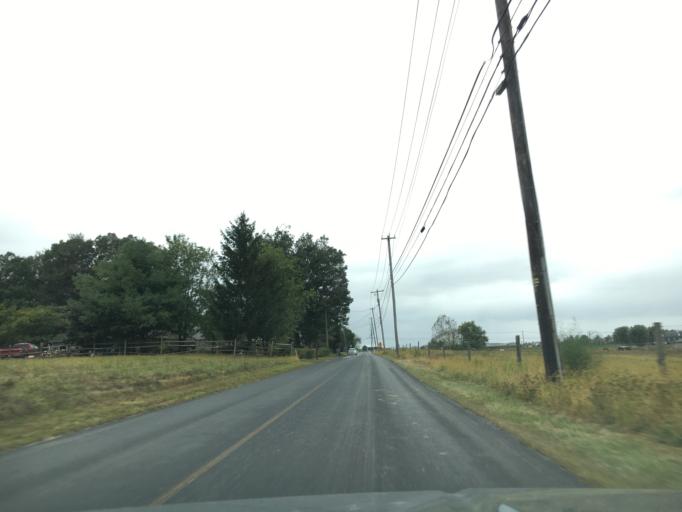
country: US
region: Pennsylvania
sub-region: Lancaster County
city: Christiana
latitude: 39.9380
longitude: -76.0316
